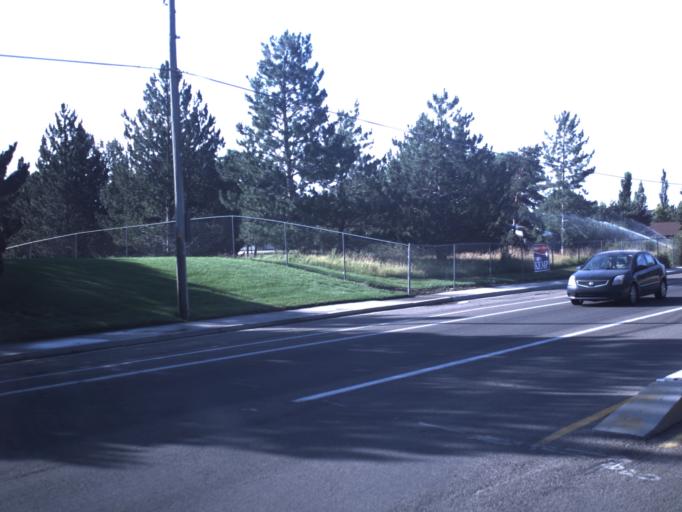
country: US
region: Utah
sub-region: Utah County
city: Cedar Hills
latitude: 40.4223
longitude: -111.7865
